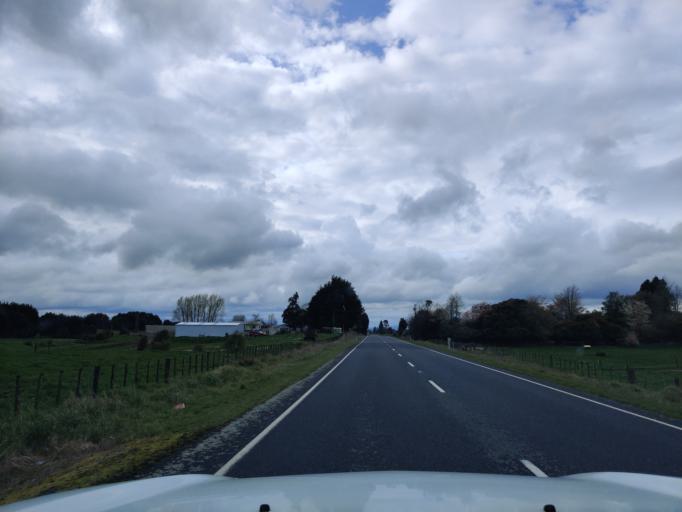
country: NZ
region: Waikato
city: Turangi
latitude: -39.0426
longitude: 175.3833
